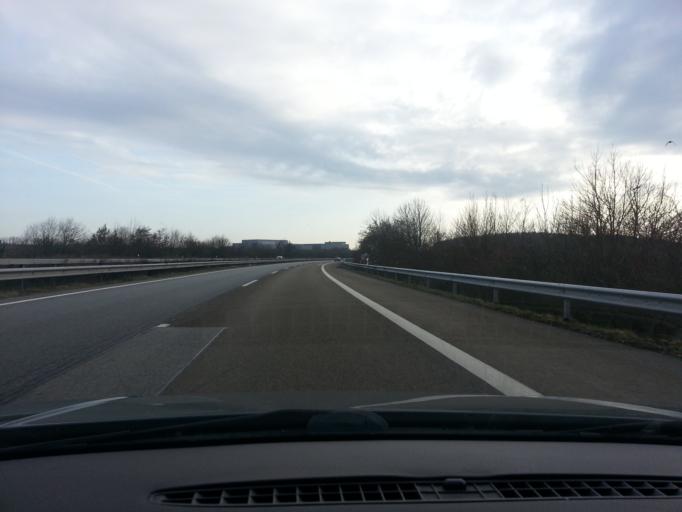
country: DE
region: Rheinland-Pfalz
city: Contwig
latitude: 49.2283
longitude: 7.4318
